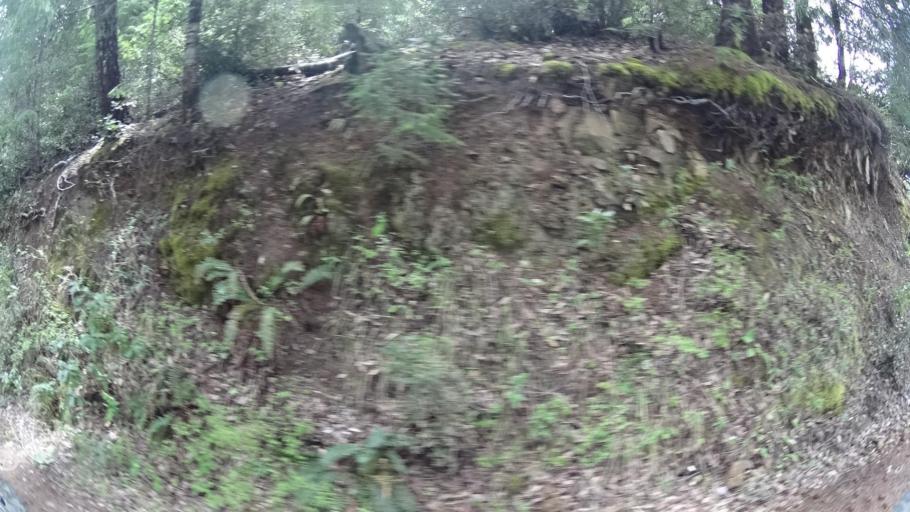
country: US
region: California
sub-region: Humboldt County
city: Blue Lake
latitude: 40.8808
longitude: -123.8816
